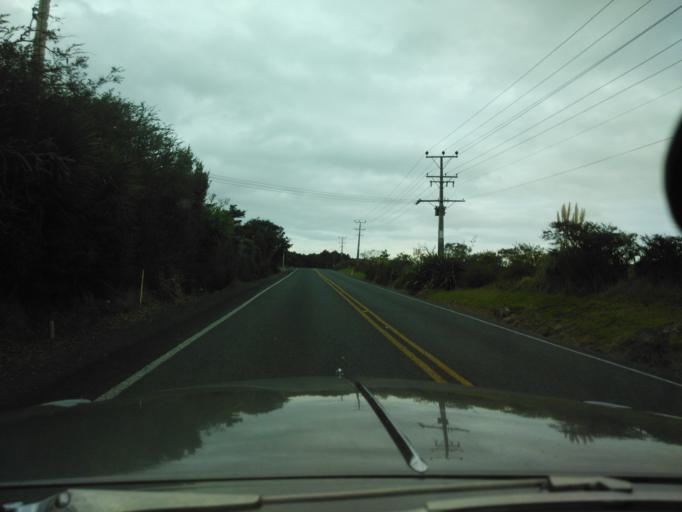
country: NZ
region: Auckland
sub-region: Auckland
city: Parakai
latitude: -36.6347
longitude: 174.5370
